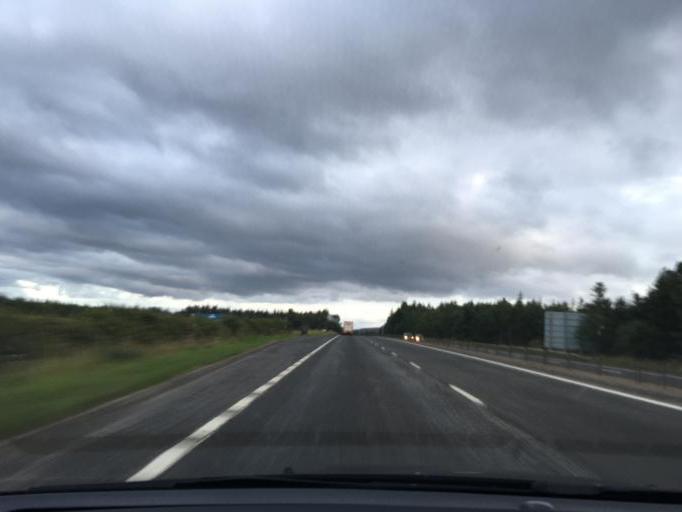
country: GB
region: Scotland
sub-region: Highland
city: Inverness
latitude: 57.4473
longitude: -4.1530
